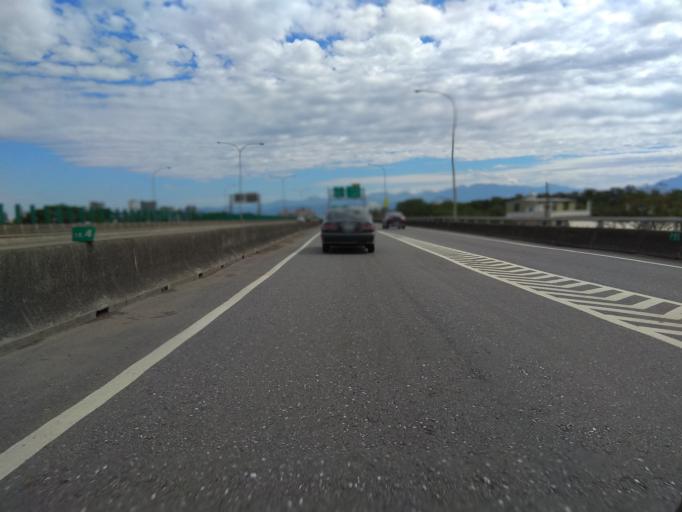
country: TW
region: Taiwan
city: Daxi
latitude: 24.9345
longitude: 121.1924
